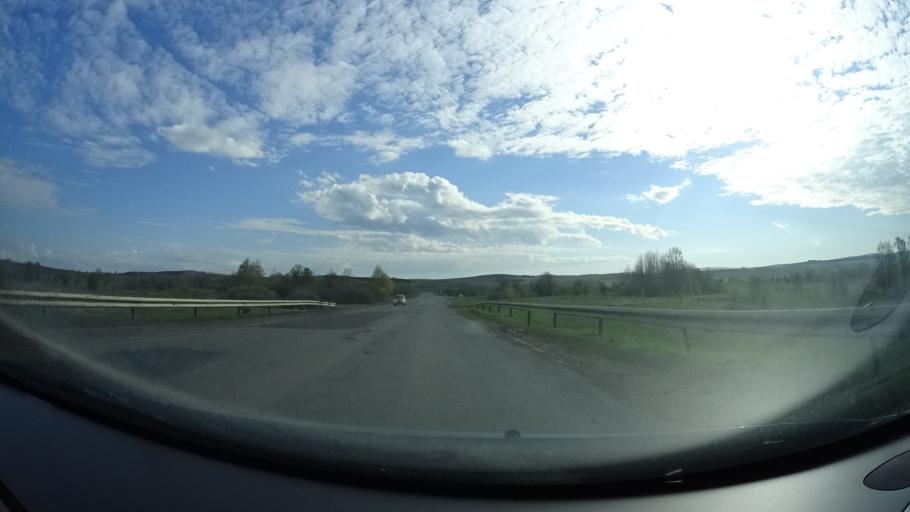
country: RU
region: Bashkortostan
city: Blagoveshchensk
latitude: 55.1070
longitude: 55.8312
